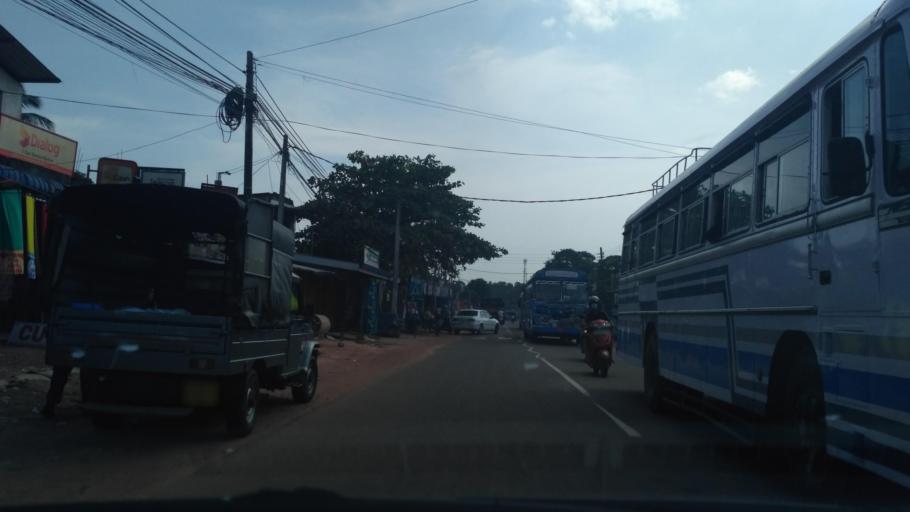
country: LK
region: North Western
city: Kuliyapitiya
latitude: 7.3510
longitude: 80.0312
